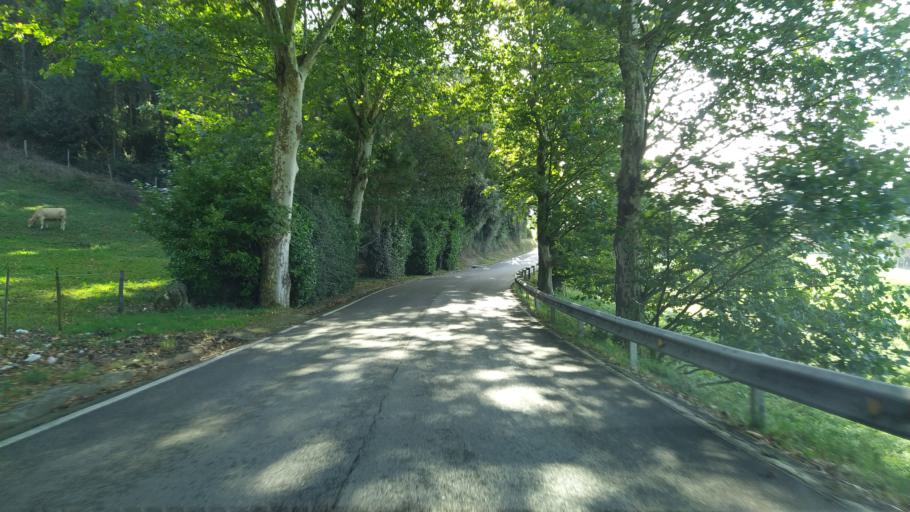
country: ES
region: Cantabria
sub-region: Provincia de Cantabria
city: Santa Cruz de Bezana
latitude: 43.4493
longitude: -3.9272
